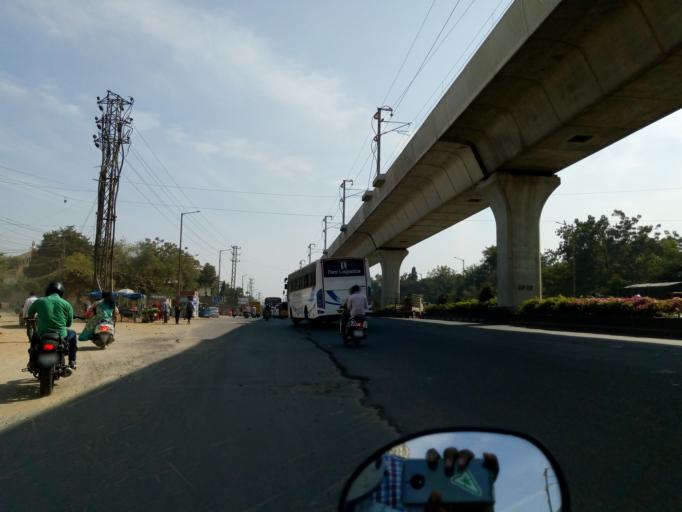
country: IN
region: Telangana
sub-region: Rangareddi
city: Uppal Kalan
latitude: 17.4061
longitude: 78.5555
